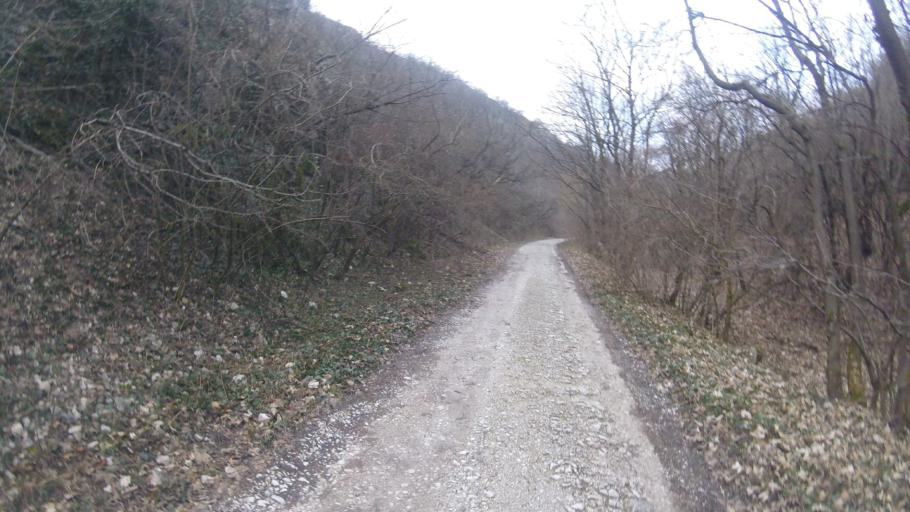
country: HU
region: Borsod-Abauj-Zemplen
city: Bogacs
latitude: 47.9595
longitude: 20.5318
